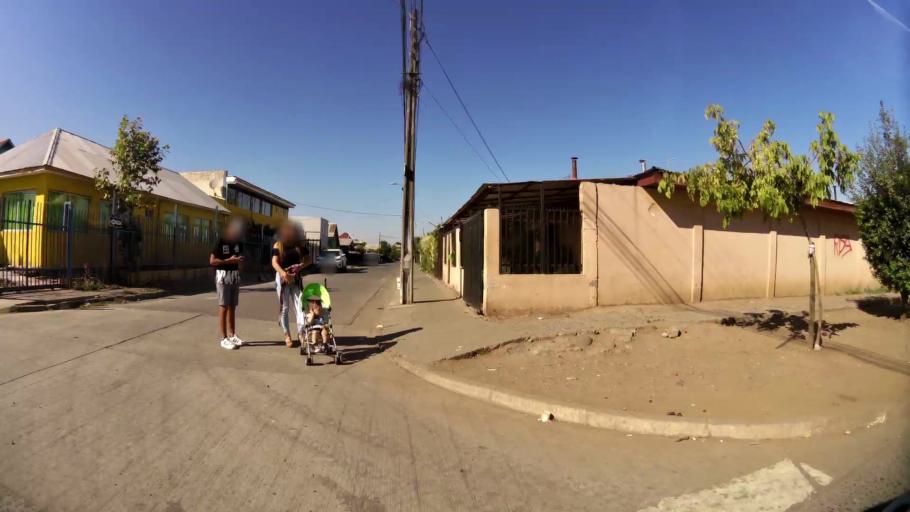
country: CL
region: Maule
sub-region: Provincia de Curico
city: Curico
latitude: -34.9976
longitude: -71.2537
